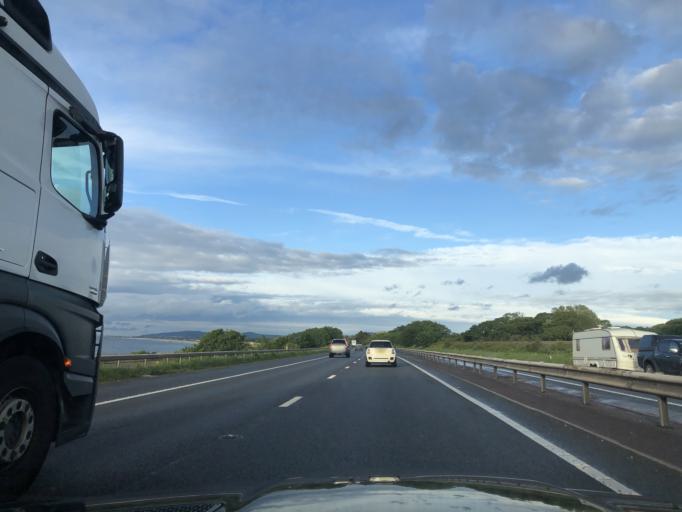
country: GB
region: Wales
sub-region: Conwy
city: Abergele
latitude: 53.2893
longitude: -3.6210
